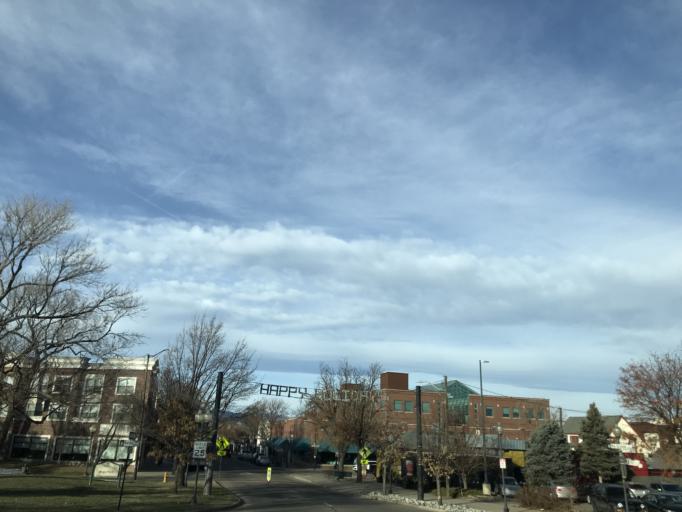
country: US
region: Colorado
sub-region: Arapahoe County
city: Littleton
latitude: 39.6137
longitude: -105.0142
